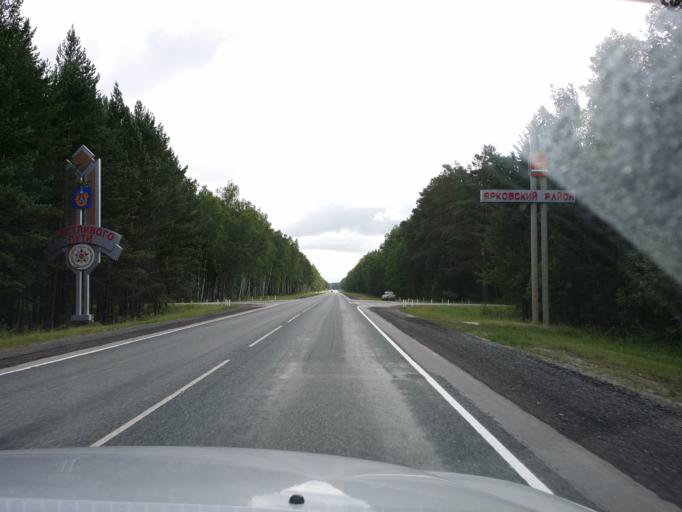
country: RU
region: Tjumen
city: Yalutorovsk
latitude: 57.1551
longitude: 66.4827
